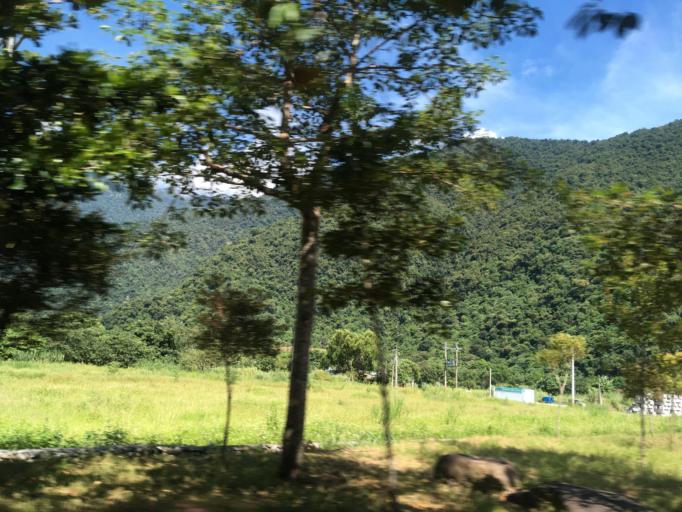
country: TW
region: Taiwan
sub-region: Yilan
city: Yilan
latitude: 24.4398
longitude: 121.7649
